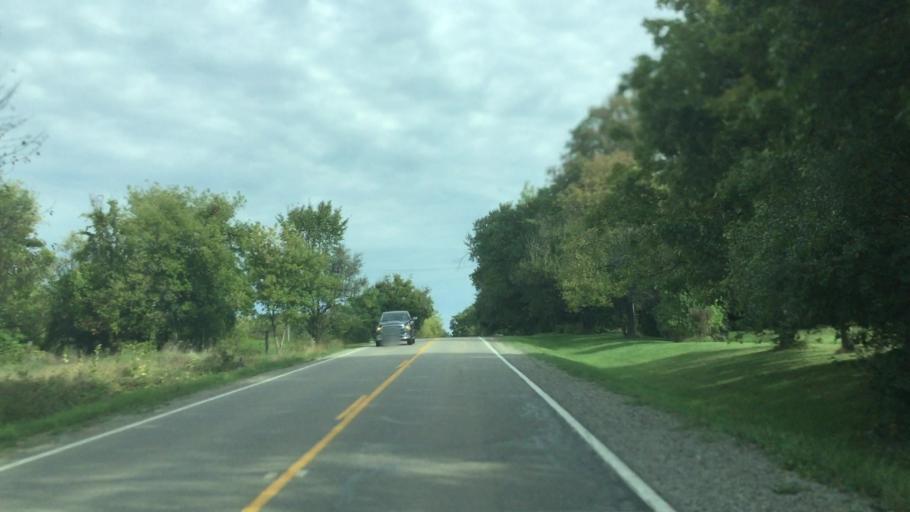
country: US
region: Michigan
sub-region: Livingston County
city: Howell
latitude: 42.6524
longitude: -83.8763
